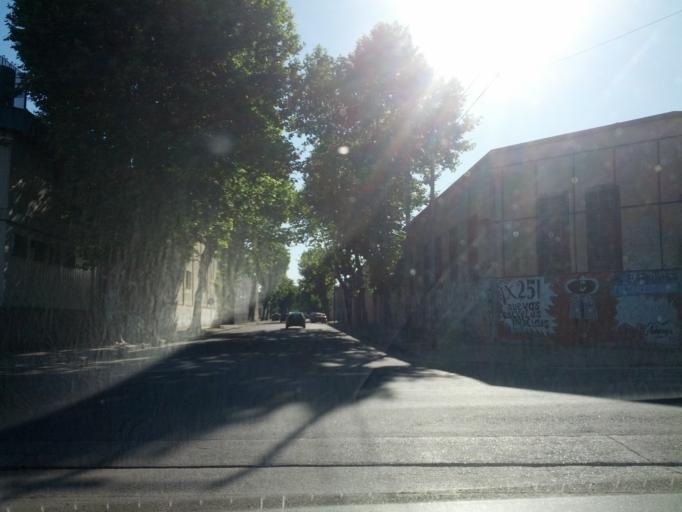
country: AR
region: Buenos Aires F.D.
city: Buenos Aires
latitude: -34.6407
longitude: -58.4036
